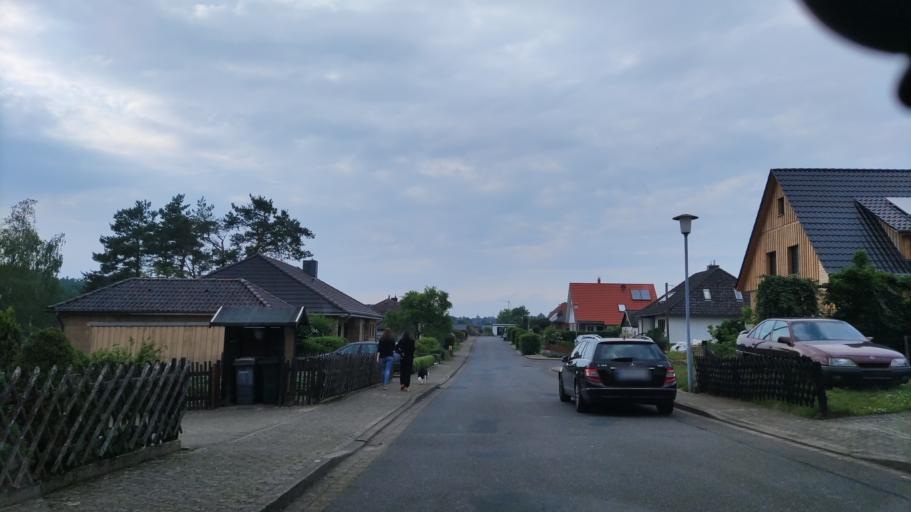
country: DE
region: Lower Saxony
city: Suderburg
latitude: 52.8942
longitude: 10.4373
